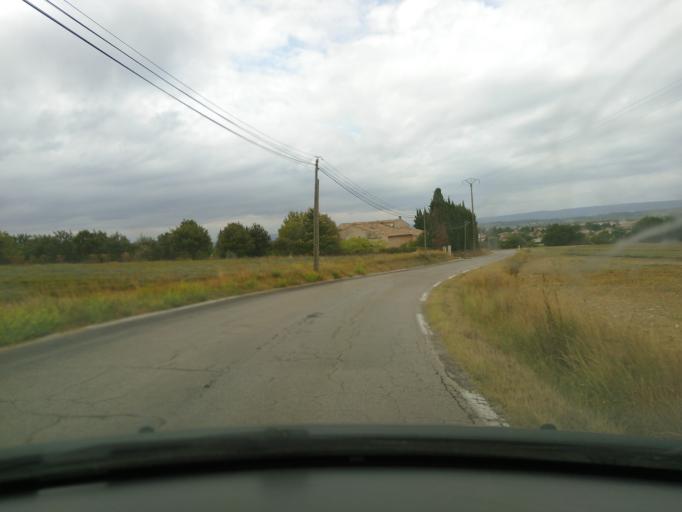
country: FR
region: Provence-Alpes-Cote d'Azur
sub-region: Departement du Vaucluse
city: Valreas
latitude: 44.3754
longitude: 5.0058
